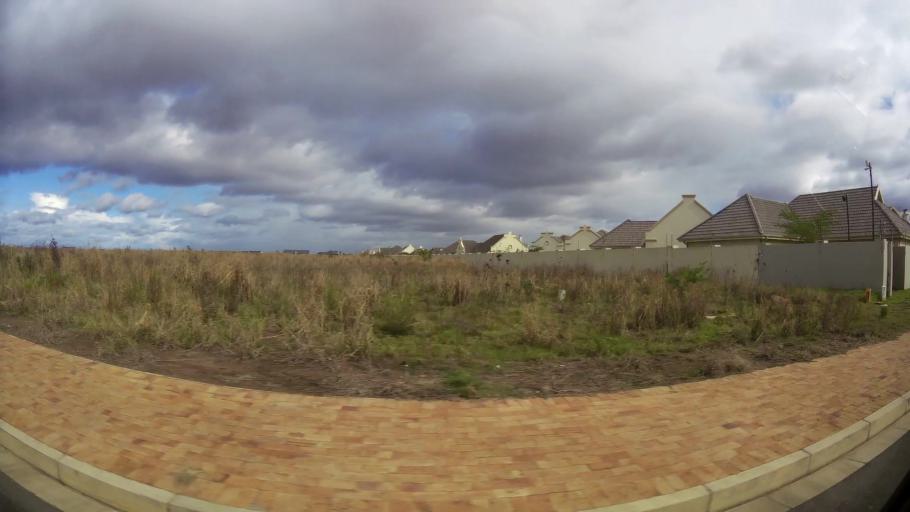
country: ZA
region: Western Cape
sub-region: Eden District Municipality
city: George
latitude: -33.9847
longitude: 22.4983
